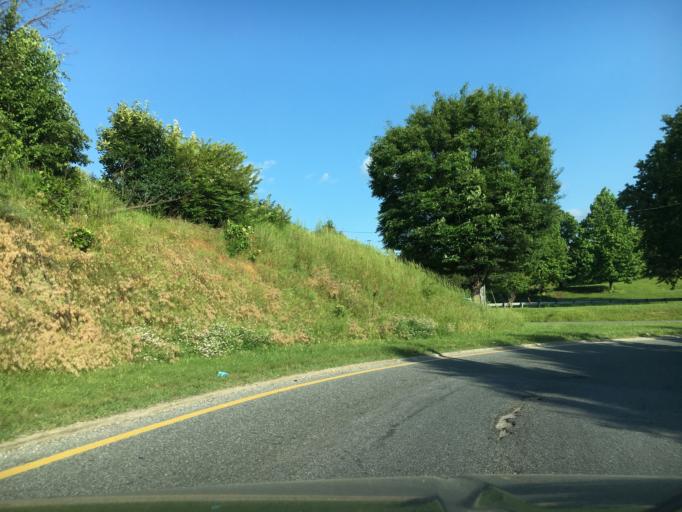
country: US
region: Virginia
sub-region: City of Lynchburg
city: West Lynchburg
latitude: 37.3667
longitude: -79.1819
